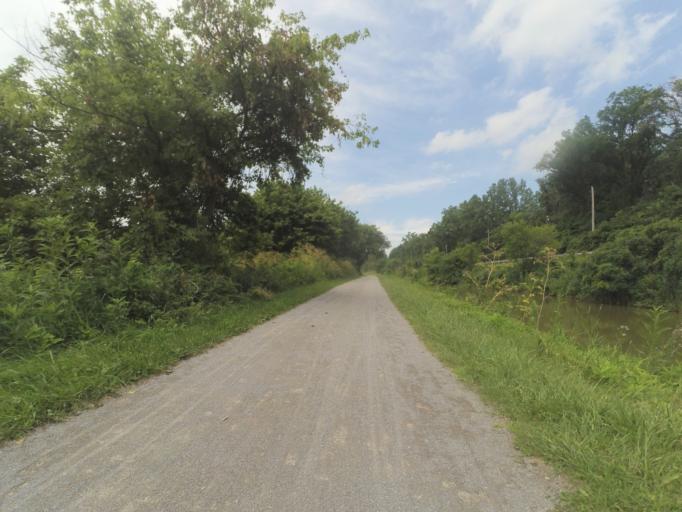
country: US
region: Ohio
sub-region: Cuyahoga County
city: Valley View
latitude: 41.3875
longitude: -81.6224
